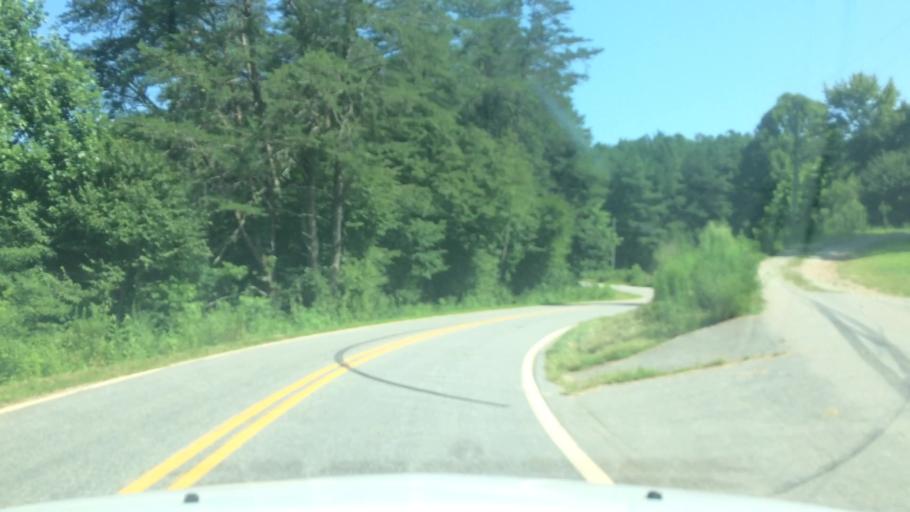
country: US
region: North Carolina
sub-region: Alexander County
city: Taylorsville
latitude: 35.9968
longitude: -81.2701
